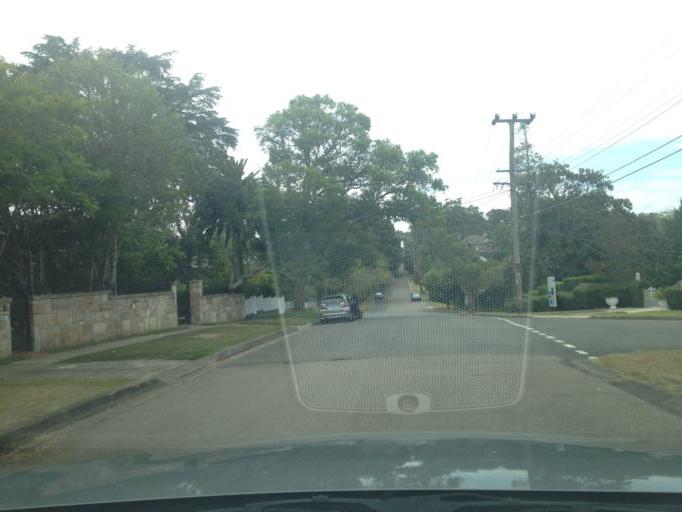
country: AU
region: New South Wales
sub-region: Ku-ring-gai
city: Killara
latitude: -33.7642
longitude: 151.1718
